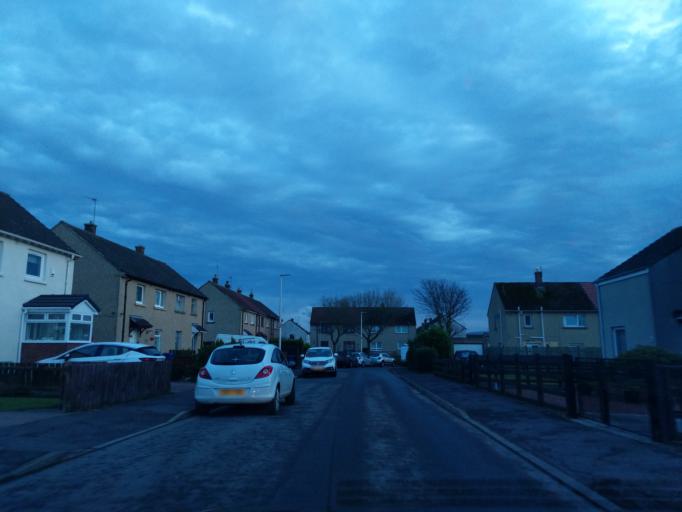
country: GB
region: Scotland
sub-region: Midlothian
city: Loanhead
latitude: 55.8709
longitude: -3.1820
